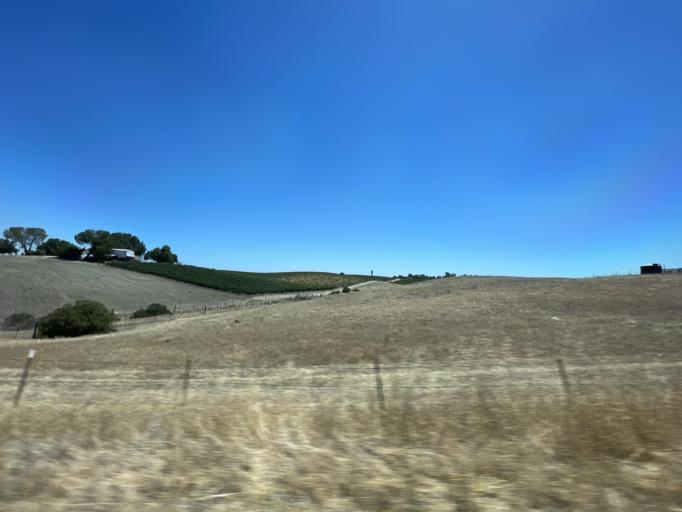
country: US
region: California
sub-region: San Luis Obispo County
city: Paso Robles
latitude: 35.6446
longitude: -120.5784
